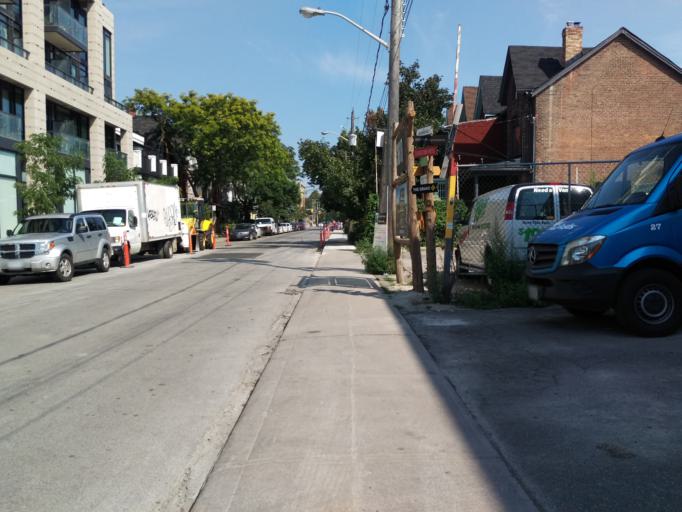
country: CA
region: Ontario
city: Toronto
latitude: 43.6416
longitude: -79.4217
